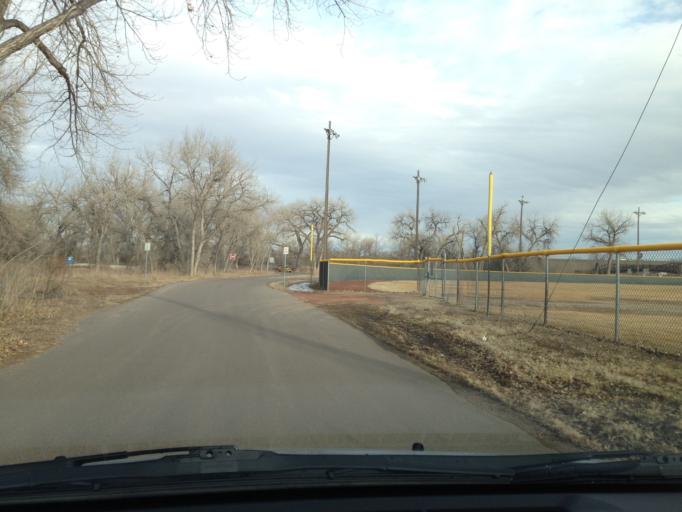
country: US
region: Colorado
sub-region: Weld County
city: Fort Lupton
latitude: 40.0821
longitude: -104.8238
